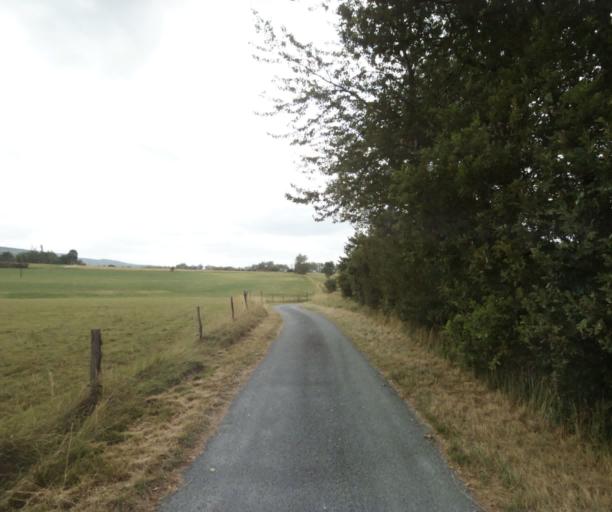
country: FR
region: Midi-Pyrenees
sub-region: Departement du Tarn
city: Soreze
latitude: 43.4638
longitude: 2.0857
